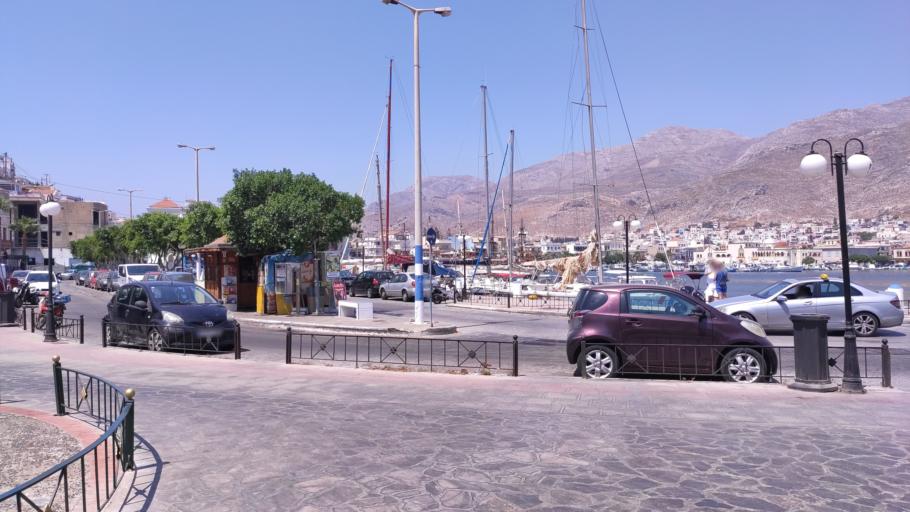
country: GR
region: South Aegean
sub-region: Nomos Dodekanisou
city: Kalymnos
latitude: 36.9465
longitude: 26.9843
